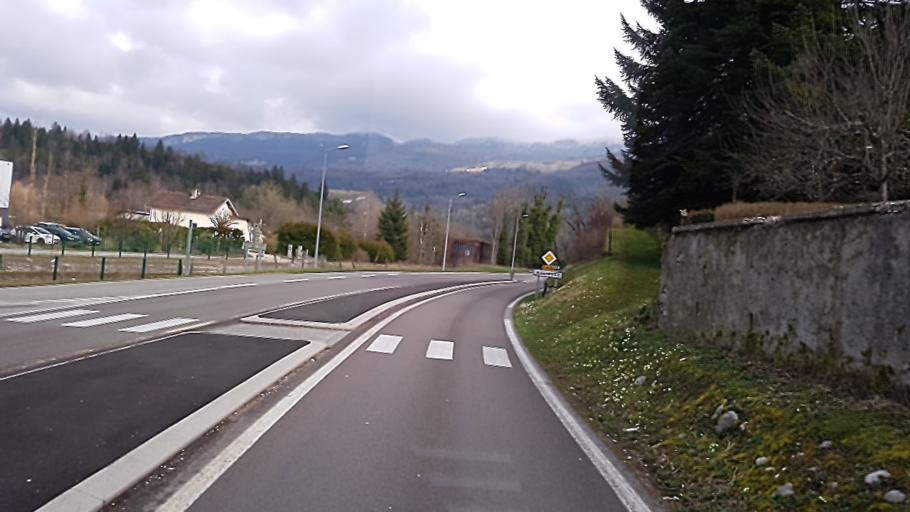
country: FR
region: Franche-Comte
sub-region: Departement du Jura
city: Lavans-les-Saint-Claude
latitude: 46.3567
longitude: 5.7687
